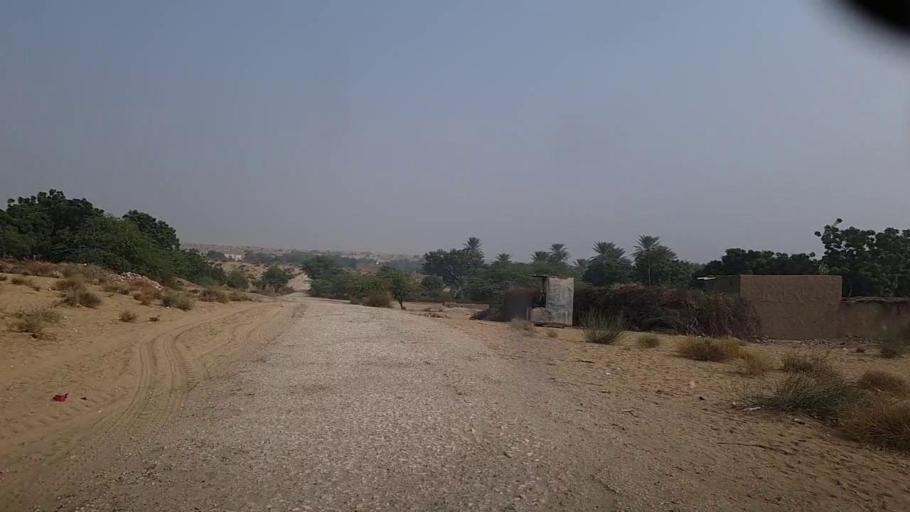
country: PK
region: Sindh
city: Bozdar
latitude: 27.0586
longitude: 68.6474
